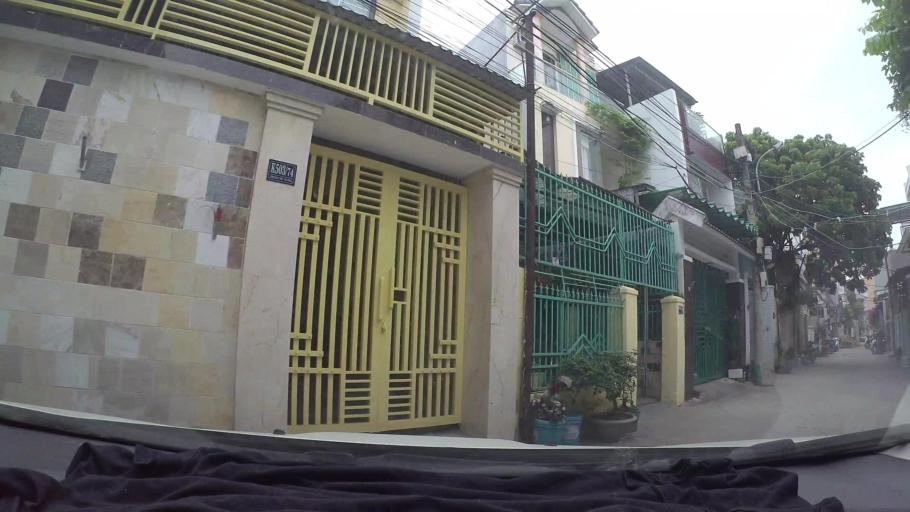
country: VN
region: Da Nang
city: Cam Le
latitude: 16.0402
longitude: 108.2062
